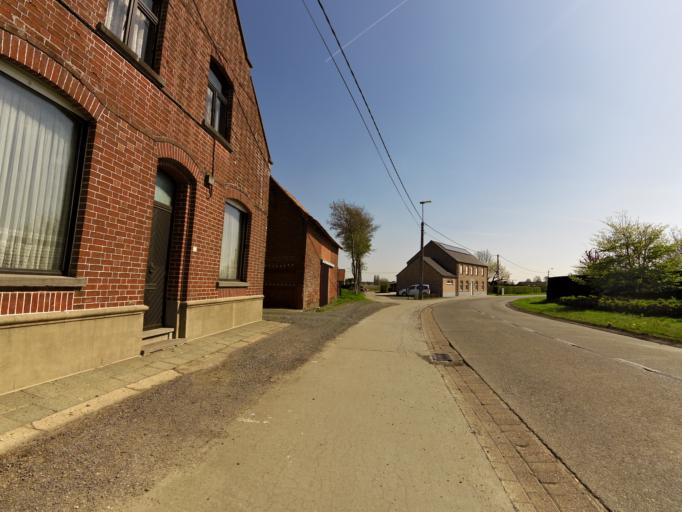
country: BE
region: Flanders
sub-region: Provincie West-Vlaanderen
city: Kortemark
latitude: 51.0453
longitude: 3.0357
